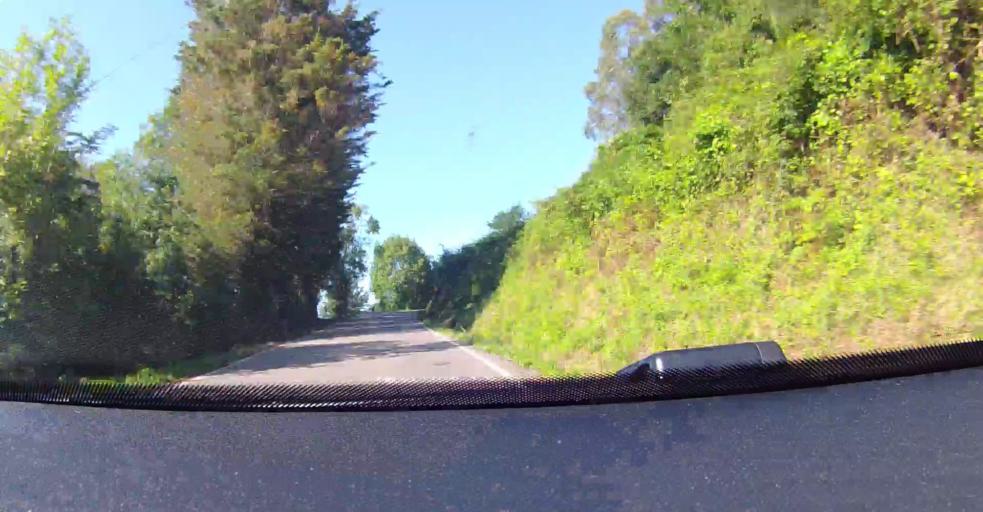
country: ES
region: Asturias
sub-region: Province of Asturias
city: Villaviciosa
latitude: 43.4826
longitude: -5.4246
